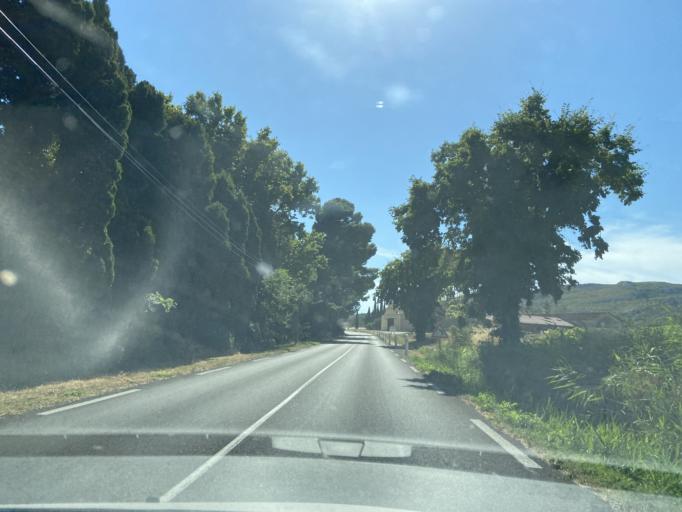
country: FR
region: Provence-Alpes-Cote d'Azur
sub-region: Departement des Bouches-du-Rhone
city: Lancon-Provence
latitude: 43.5459
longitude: 5.1403
